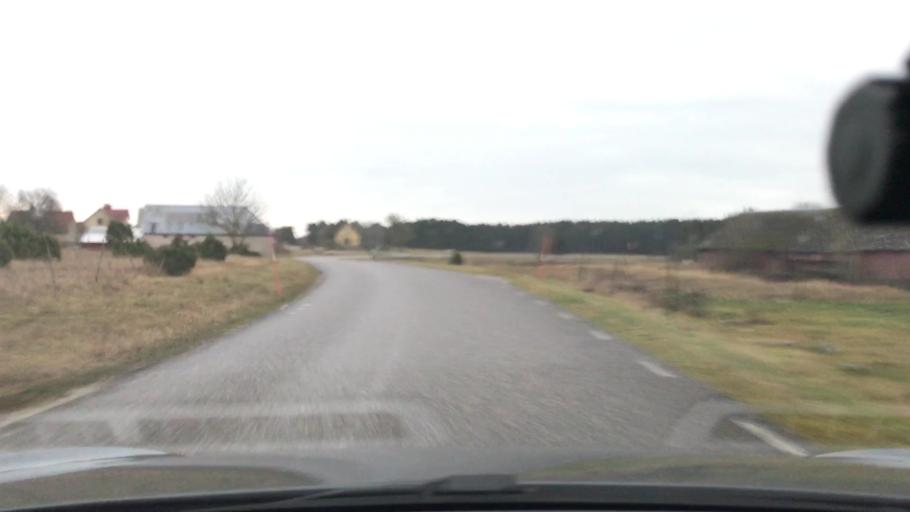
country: SE
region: Gotland
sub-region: Gotland
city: Slite
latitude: 57.3971
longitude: 18.8059
